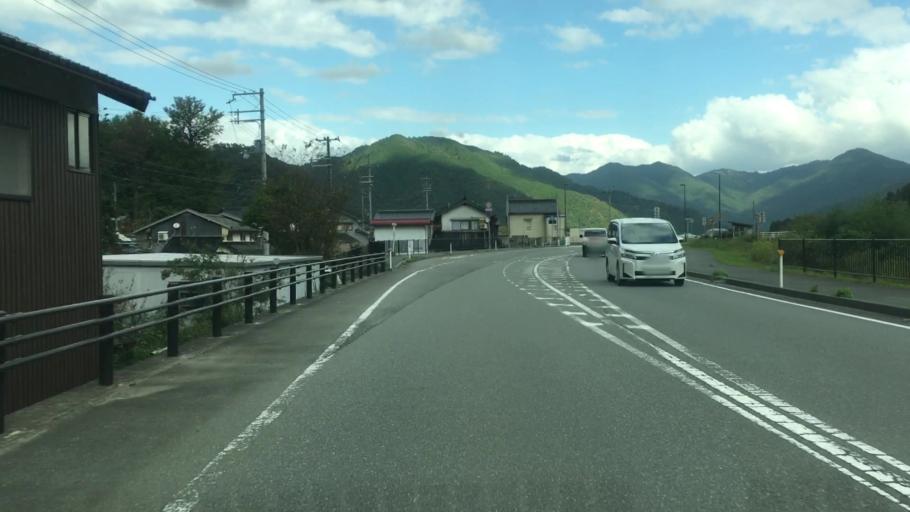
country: JP
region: Hyogo
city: Toyooka
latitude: 35.3711
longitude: 134.7635
